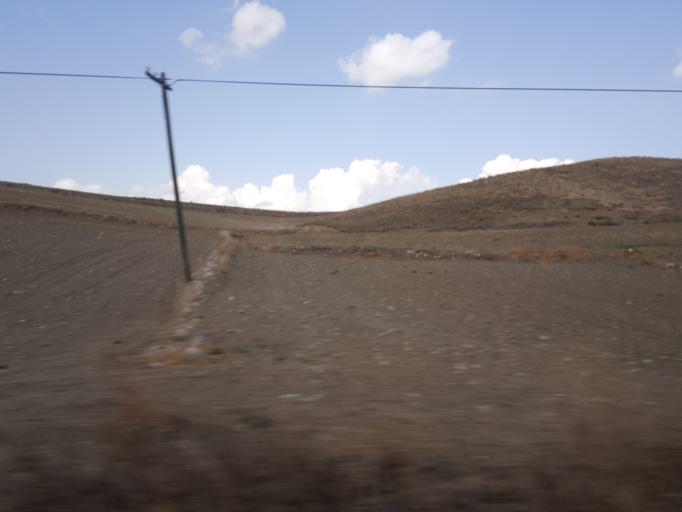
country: TR
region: Corum
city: Bogazkale
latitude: 40.1374
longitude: 34.5621
